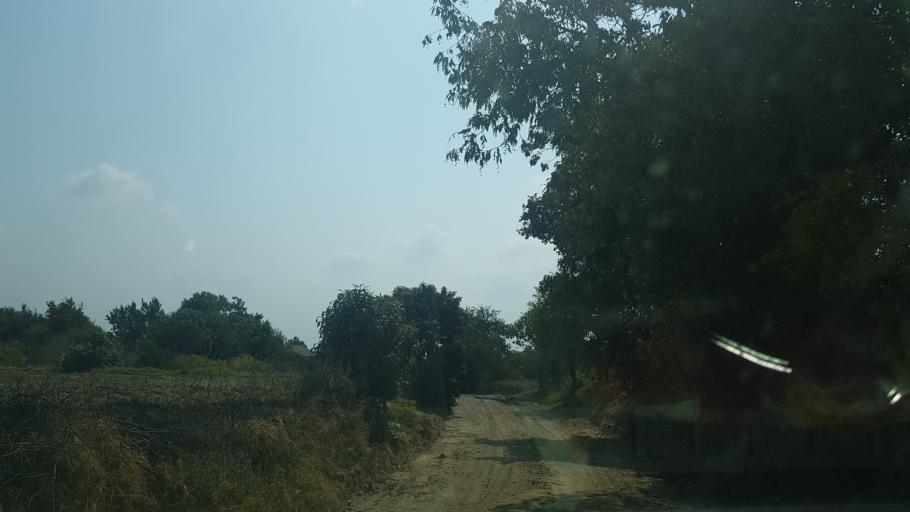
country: MX
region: Puebla
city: Domingo Arenas
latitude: 19.1295
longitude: -98.5064
